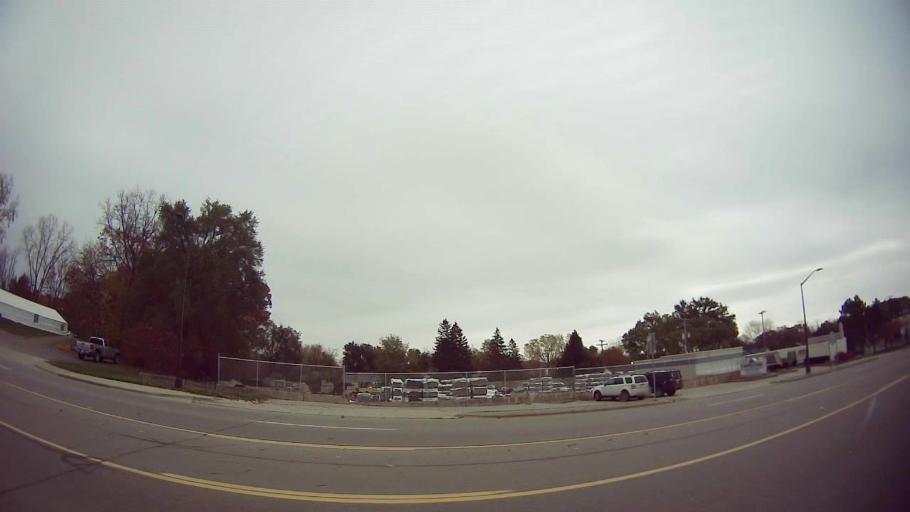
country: US
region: Michigan
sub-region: Oakland County
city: Waterford
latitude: 42.7078
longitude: -83.4060
